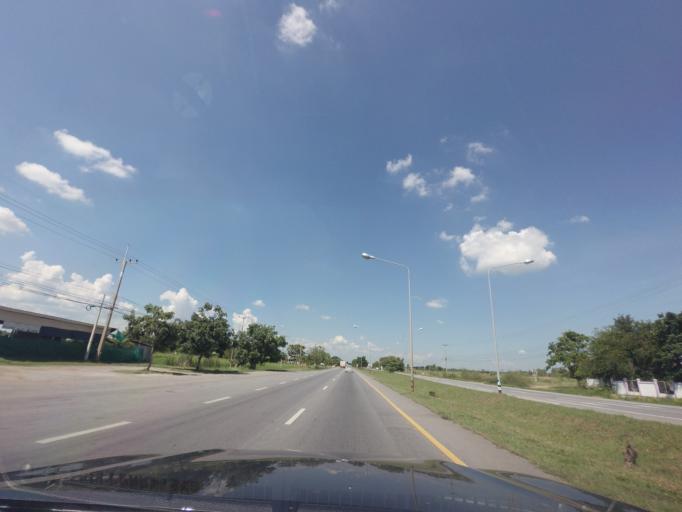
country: TH
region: Nakhon Ratchasima
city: Non Sung
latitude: 15.1272
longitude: 102.3051
